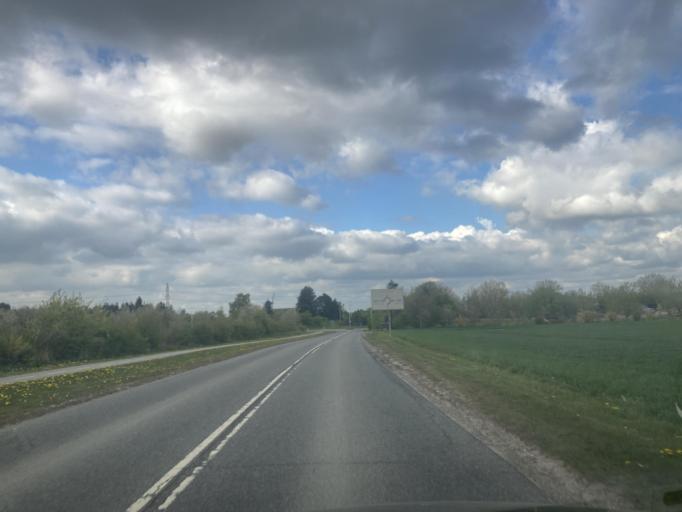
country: DK
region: Zealand
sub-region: Greve Kommune
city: Tune
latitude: 55.6057
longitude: 12.1804
